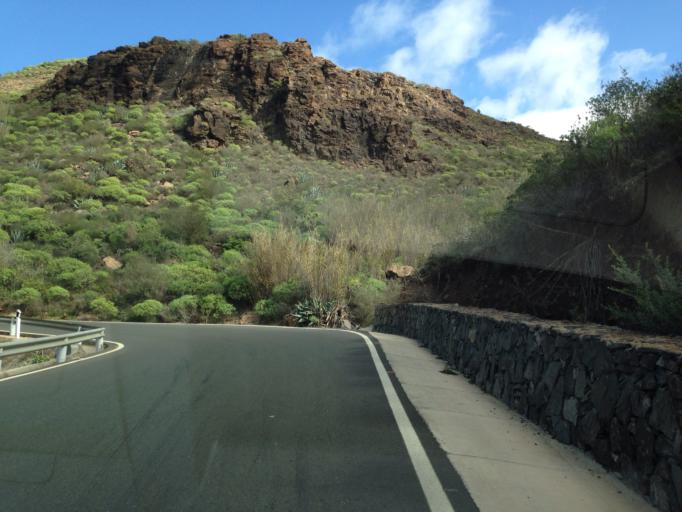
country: ES
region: Canary Islands
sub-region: Provincia de Las Palmas
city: Santa Lucia
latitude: 27.8965
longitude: -15.5630
